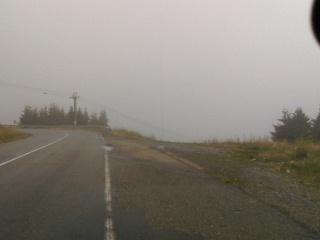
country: BG
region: Lovech
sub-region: Obshtina Troyan
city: Troyan
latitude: 42.7826
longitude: 24.6234
